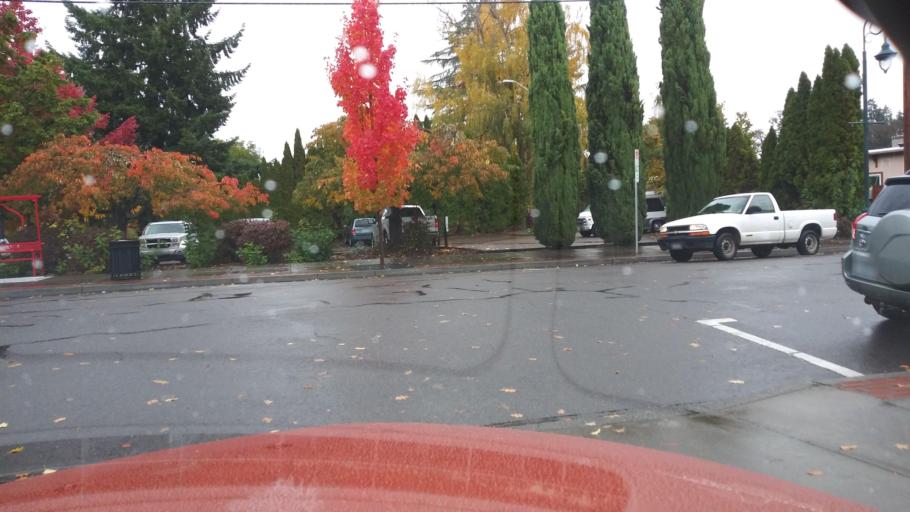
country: US
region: Oregon
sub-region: Washington County
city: Forest Grove
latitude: 45.5209
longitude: -123.1137
